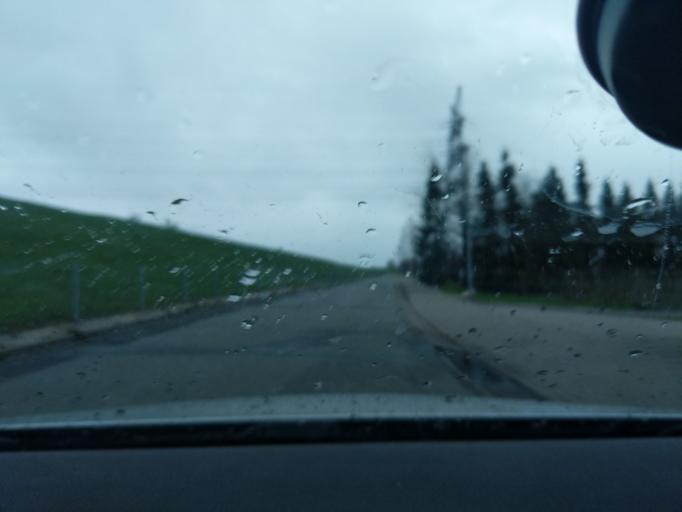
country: DE
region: Schleswig-Holstein
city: Haseldorf
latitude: 53.5906
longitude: 9.5805
